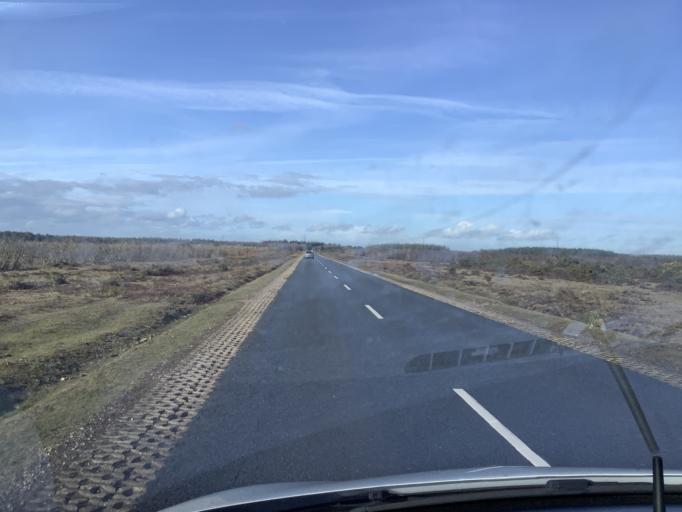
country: GB
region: England
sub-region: Hampshire
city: Hythe
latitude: 50.8340
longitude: -1.4290
